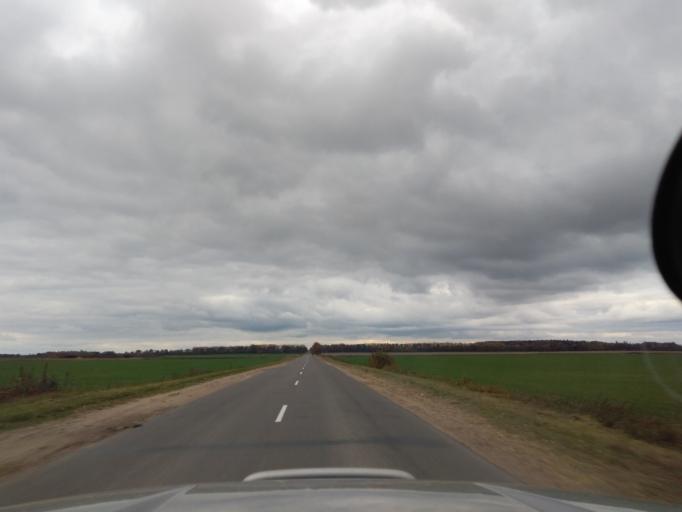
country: BY
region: Minsk
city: Slutsk
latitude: 53.2101
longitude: 27.3661
